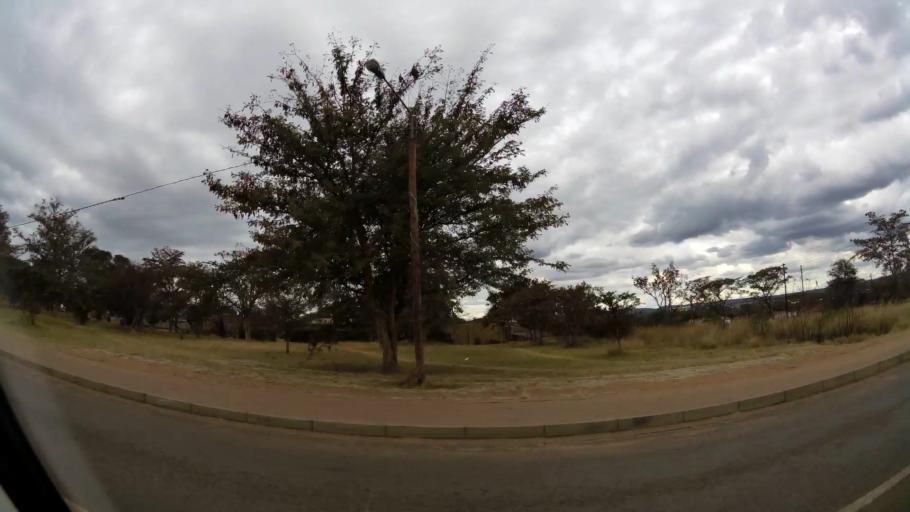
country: ZA
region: Limpopo
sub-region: Waterberg District Municipality
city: Modimolle
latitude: -24.6974
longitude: 28.4197
